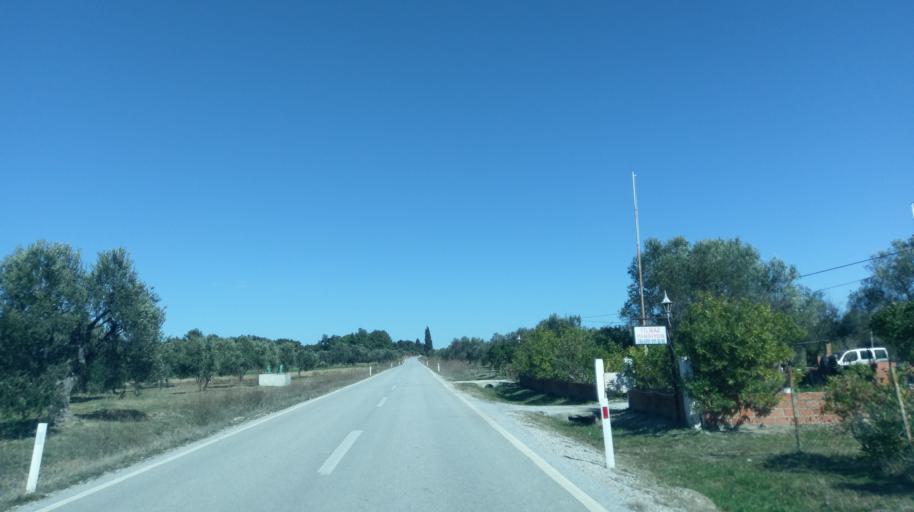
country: TR
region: Canakkale
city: Intepe
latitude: 40.0725
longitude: 26.2110
